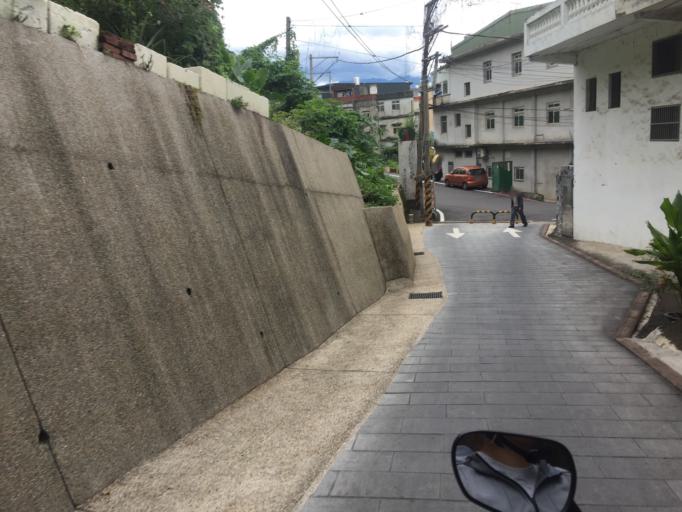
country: TW
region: Taiwan
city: Daxi
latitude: 24.7890
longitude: 121.1759
